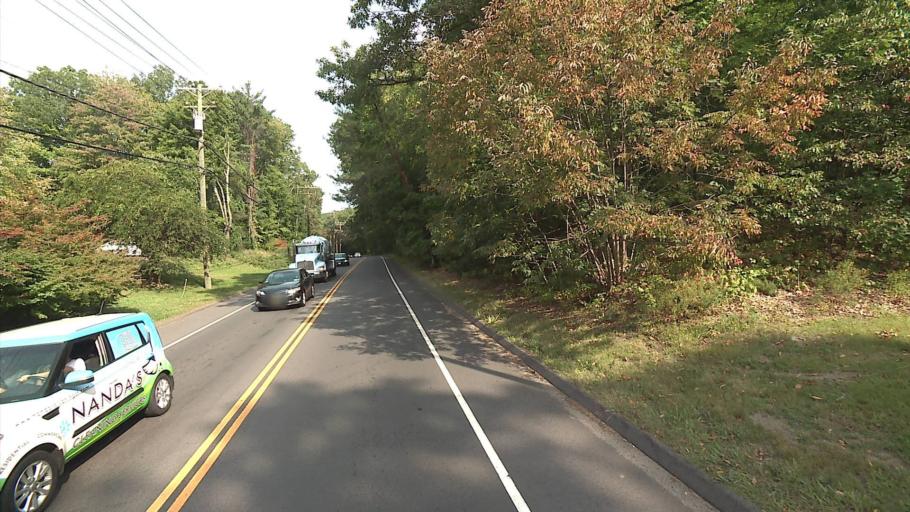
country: US
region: Connecticut
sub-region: Fairfield County
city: New Canaan
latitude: 41.1460
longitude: -73.4801
